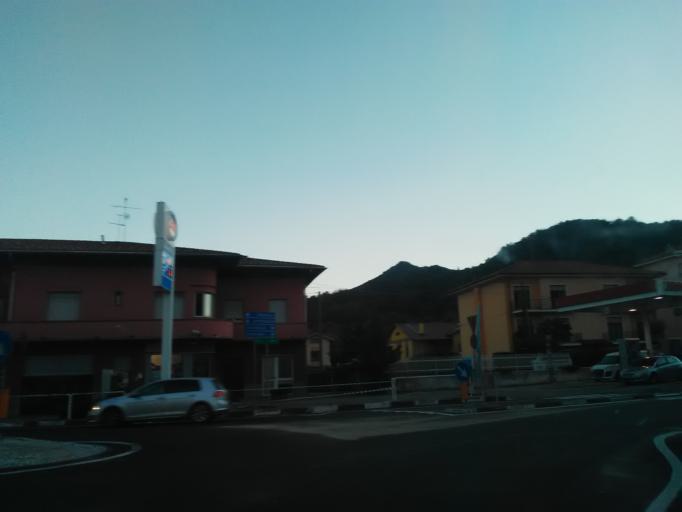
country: IT
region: Piedmont
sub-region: Provincia di Vercelli
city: Serravalle Sesia
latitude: 45.6976
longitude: 8.2869
